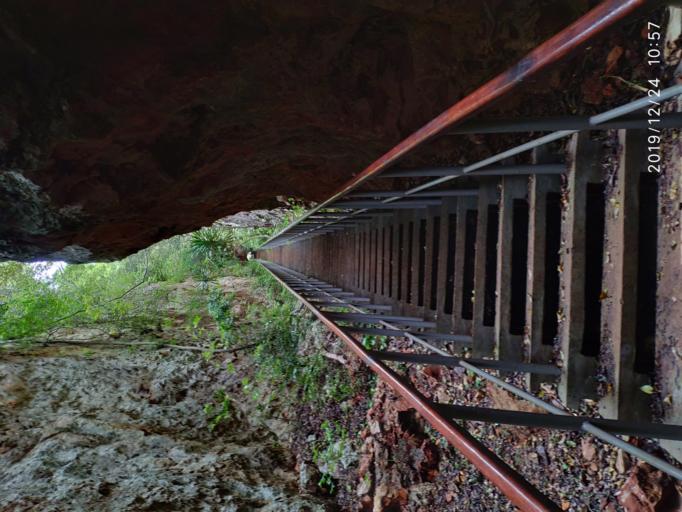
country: MG
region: Diana
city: Antsiranana
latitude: -12.2974
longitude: 49.3430
